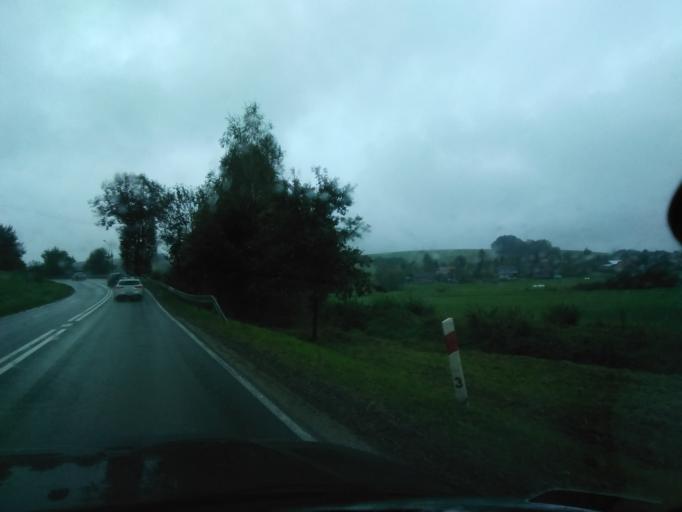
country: PL
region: Subcarpathian Voivodeship
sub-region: Powiat ropczycko-sedziszowski
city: Wielopole Skrzynskie
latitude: 49.9517
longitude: 21.5999
